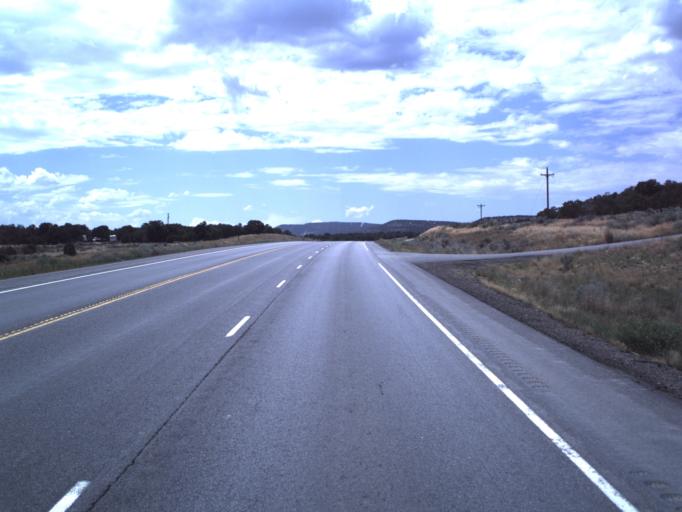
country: US
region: Utah
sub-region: Duchesne County
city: Duchesne
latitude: 40.1713
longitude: -110.5658
